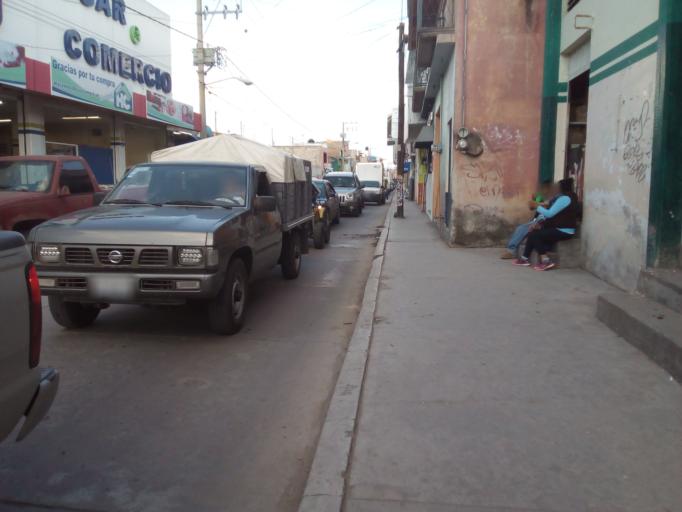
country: MX
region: Guerrero
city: San Luis de la Paz
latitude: 21.2968
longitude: -100.5241
